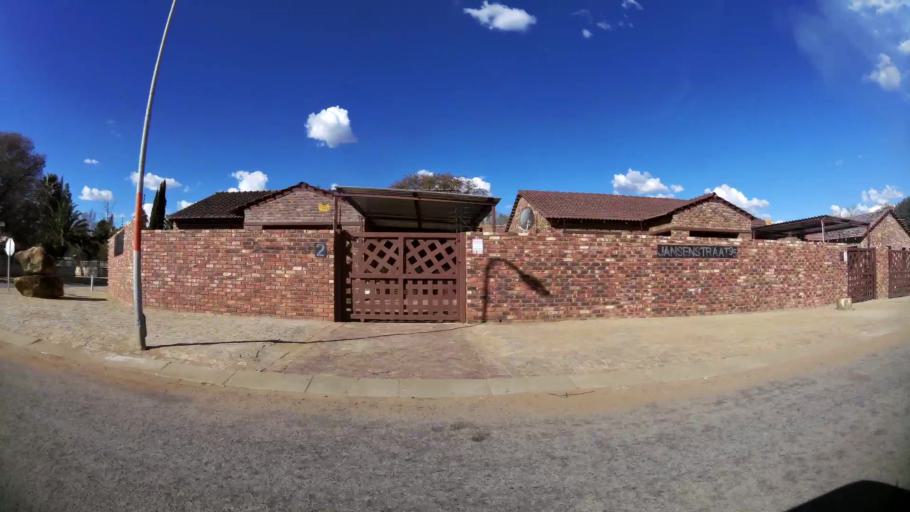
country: ZA
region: North-West
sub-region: Dr Kenneth Kaunda District Municipality
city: Klerksdorp
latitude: -26.8201
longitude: 26.6502
